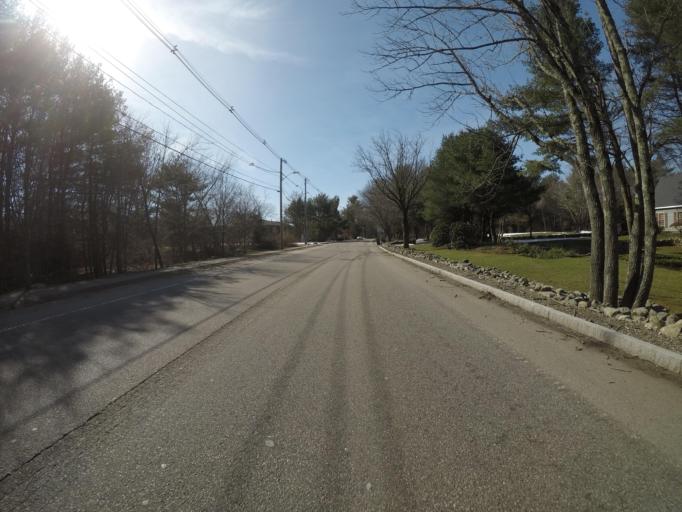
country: US
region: Massachusetts
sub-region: Bristol County
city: Easton
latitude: 42.0003
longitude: -71.1465
